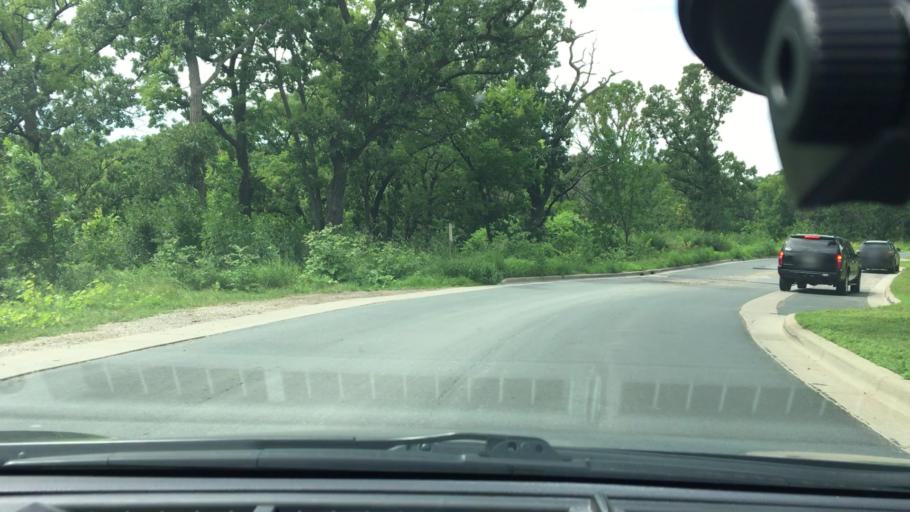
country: US
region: Minnesota
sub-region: Dakota County
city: Mendota Heights
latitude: 44.9145
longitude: -93.2065
